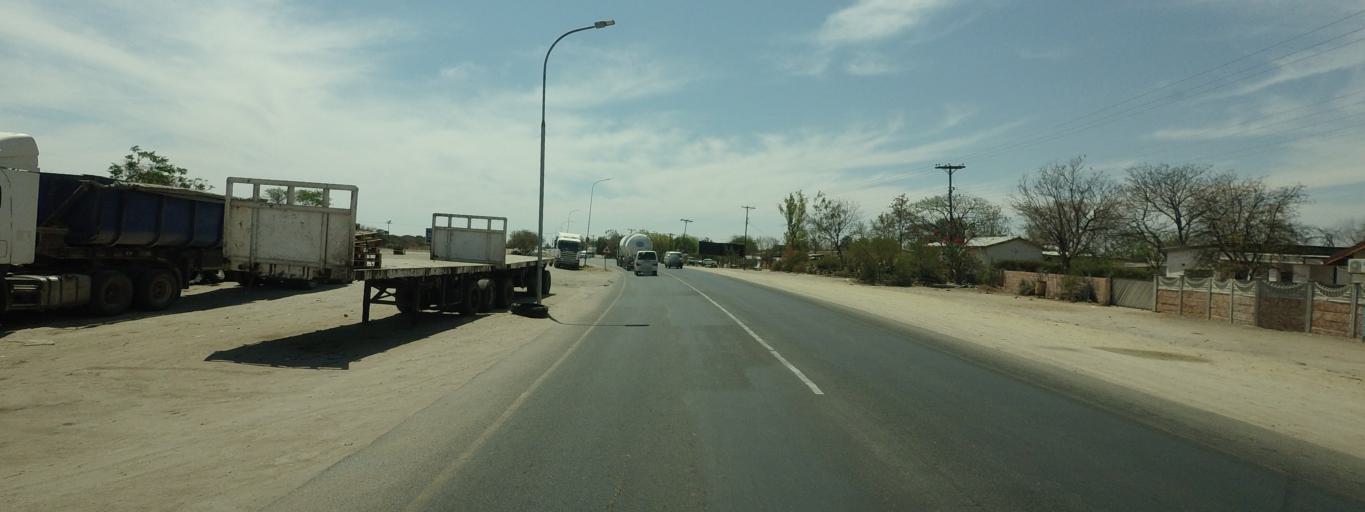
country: BW
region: North East
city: Francistown
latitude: -21.1649
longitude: 27.4940
